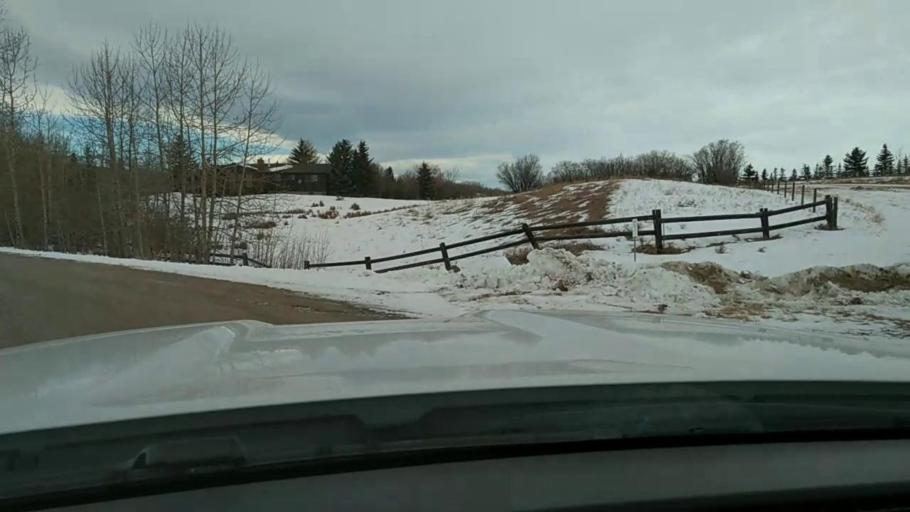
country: CA
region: Alberta
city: Cochrane
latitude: 51.2001
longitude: -114.2866
